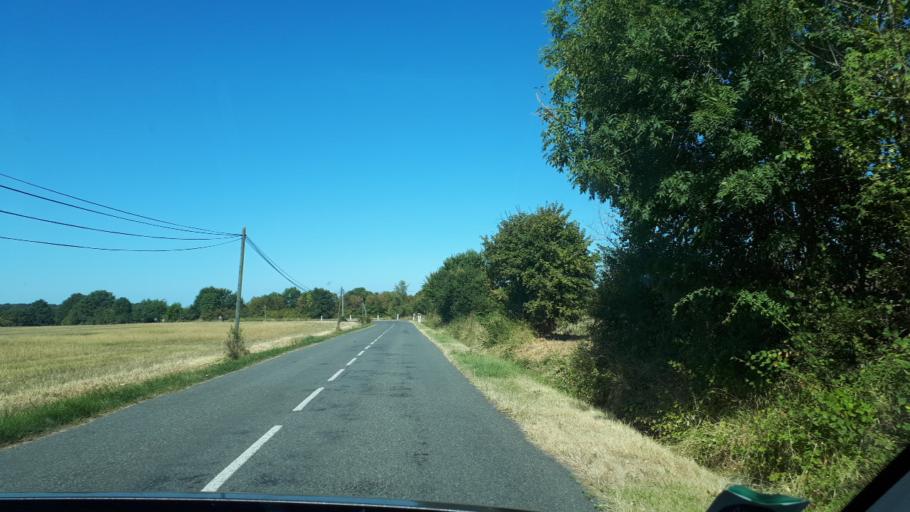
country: FR
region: Centre
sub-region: Departement du Loiret
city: Autry-le-Chatel
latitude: 47.6025
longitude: 2.5968
